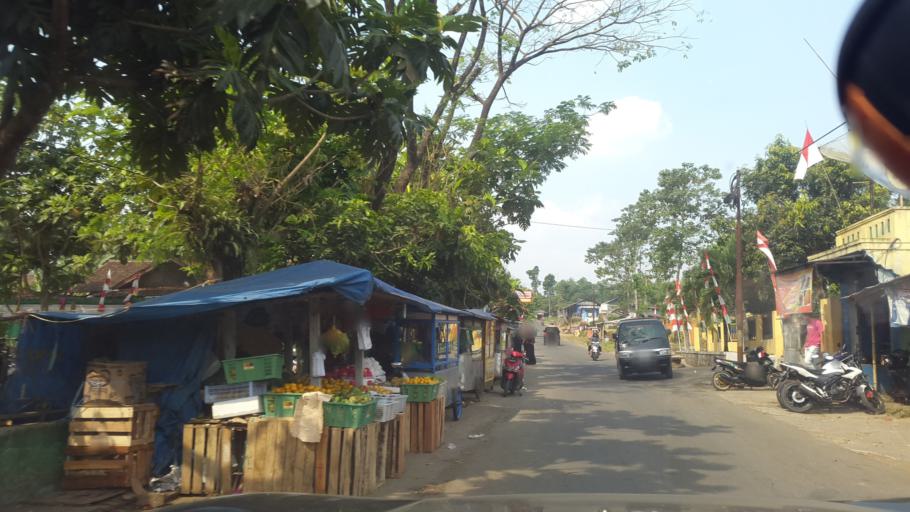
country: ID
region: West Java
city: Cicurug
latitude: -6.8245
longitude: 106.7933
